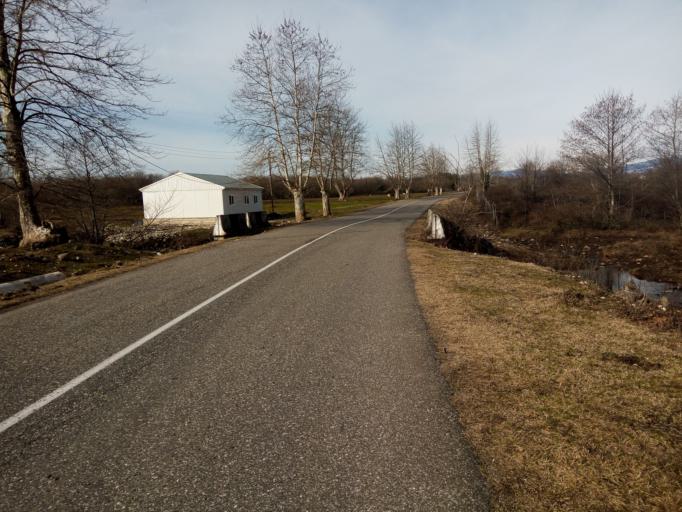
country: GE
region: Samegrelo and Zemo Svaneti
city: Mart'vili
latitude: 42.4908
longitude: 42.3330
